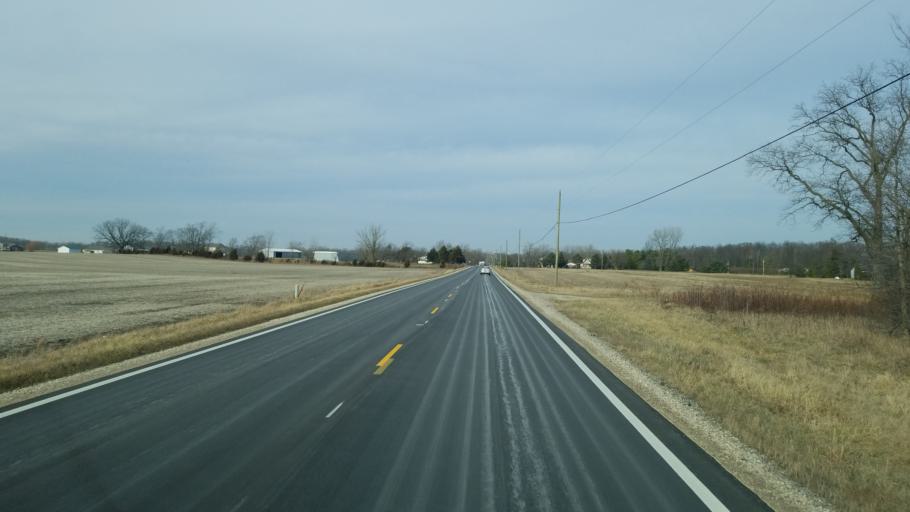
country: US
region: Ohio
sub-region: Union County
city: Richwood
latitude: 40.3666
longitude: -83.4024
